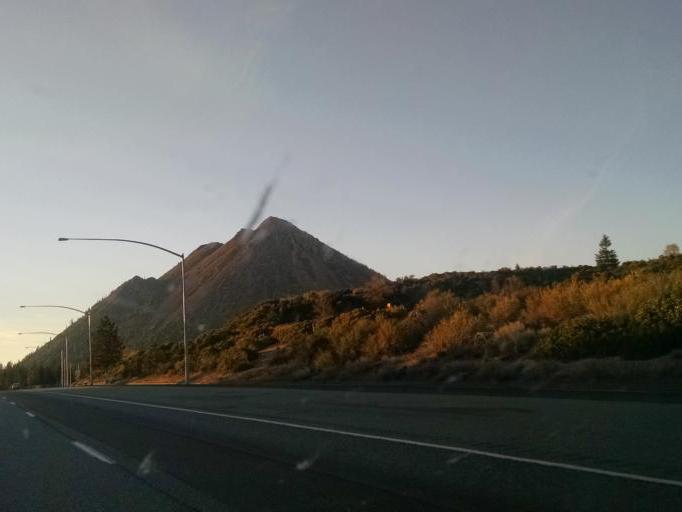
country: US
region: California
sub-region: Siskiyou County
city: Mount Shasta
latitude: 41.3366
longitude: -122.3365
